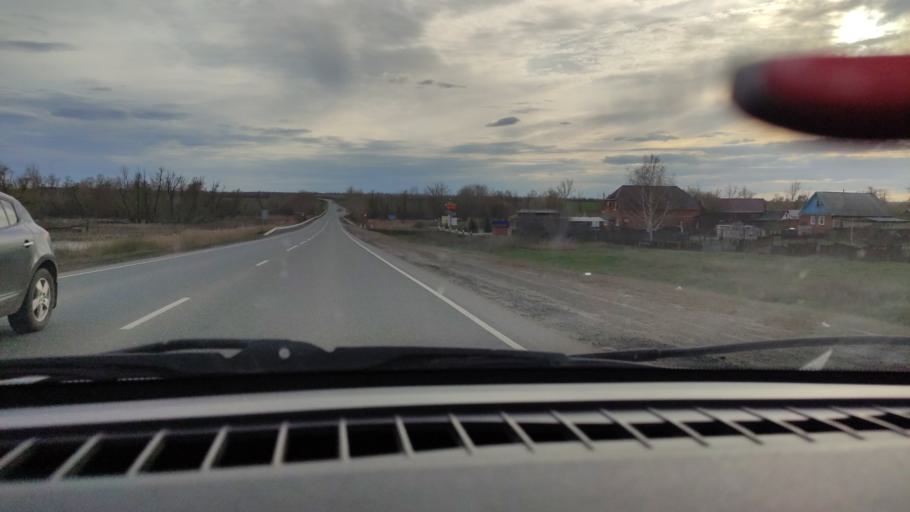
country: RU
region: Orenburg
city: Tatarskaya Kargala
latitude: 52.0249
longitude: 55.2251
